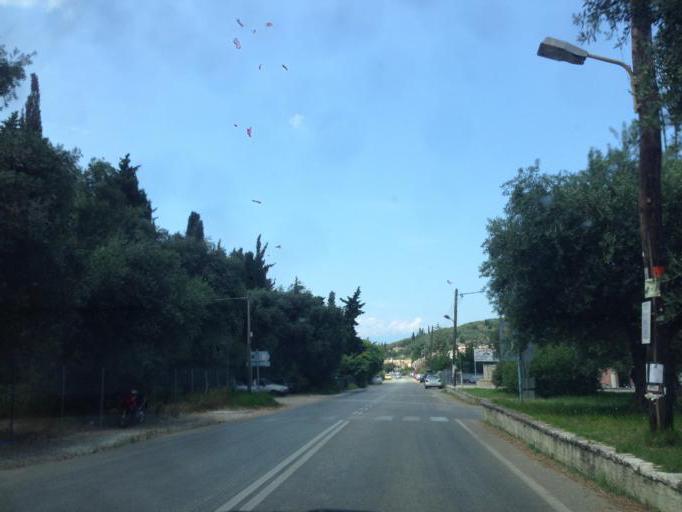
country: GR
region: Ionian Islands
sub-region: Nomos Kerkyras
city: Acharavi
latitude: 39.7855
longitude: 19.9209
